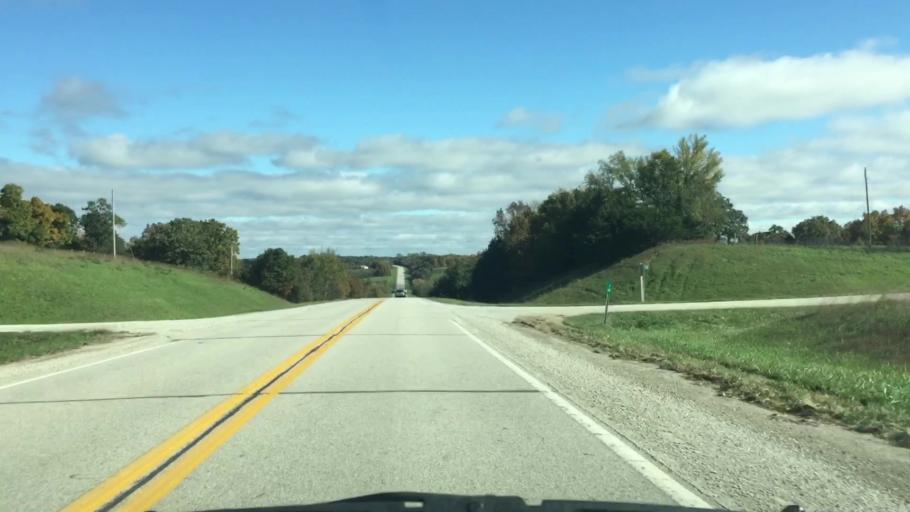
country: US
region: Iowa
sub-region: Decatur County
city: Leon
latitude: 40.6753
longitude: -93.7862
